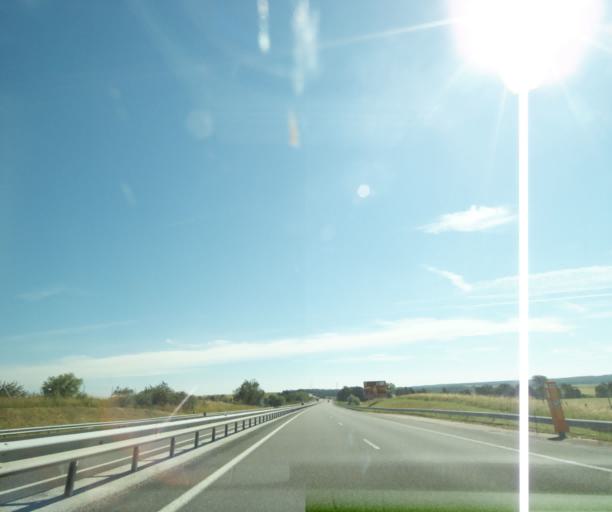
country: FR
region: Lorraine
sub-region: Departement des Vosges
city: Bulgneville
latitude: 48.1907
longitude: 5.7670
